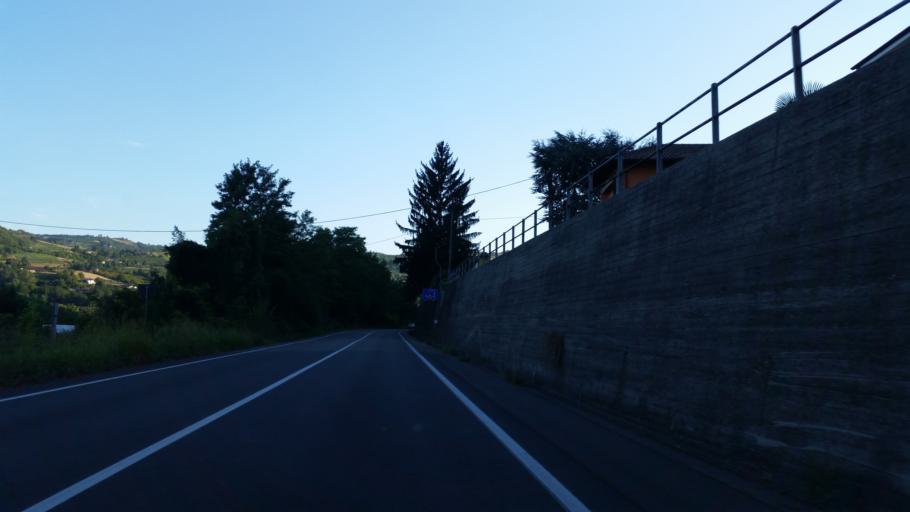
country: IT
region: Piedmont
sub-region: Provincia di Asti
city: Canelli
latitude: 44.7156
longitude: 8.2693
